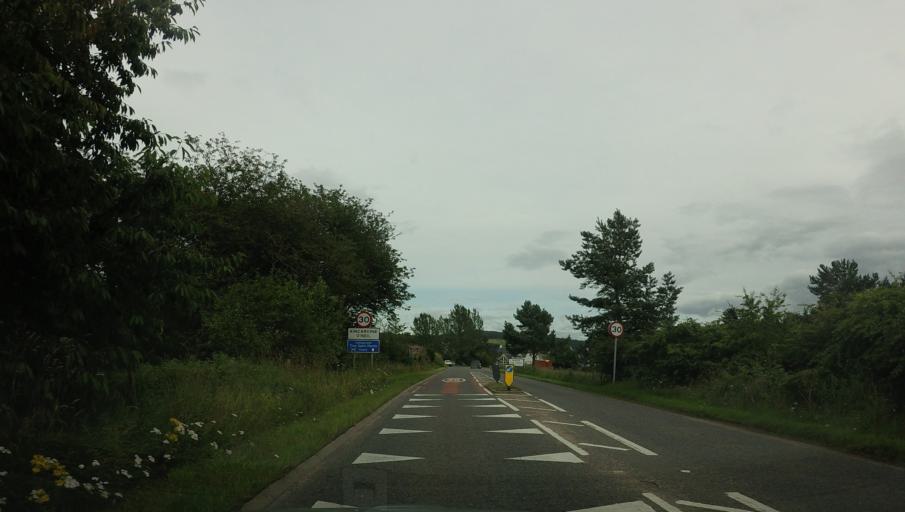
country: GB
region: Scotland
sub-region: Aberdeenshire
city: Torphins
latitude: 57.0869
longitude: -2.6845
